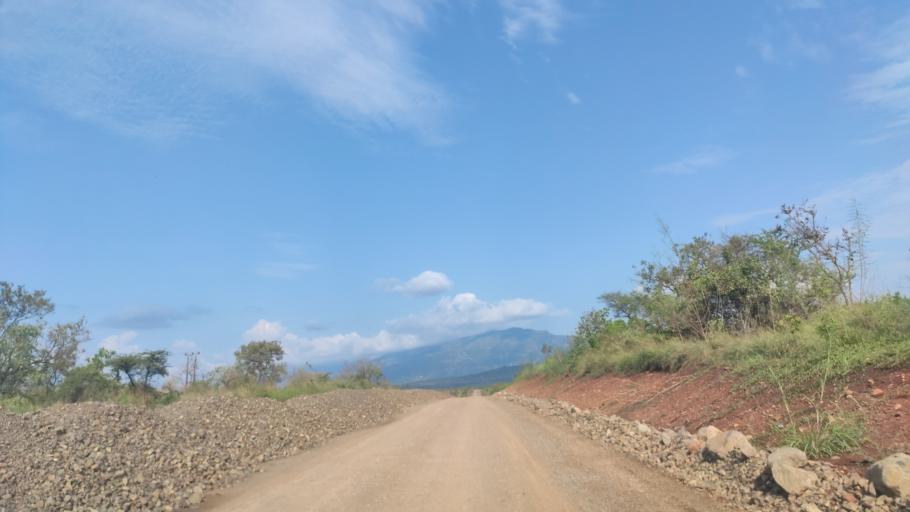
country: ET
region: Southern Nations, Nationalities, and People's Region
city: Felege Neway
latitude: 6.4245
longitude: 37.2455
